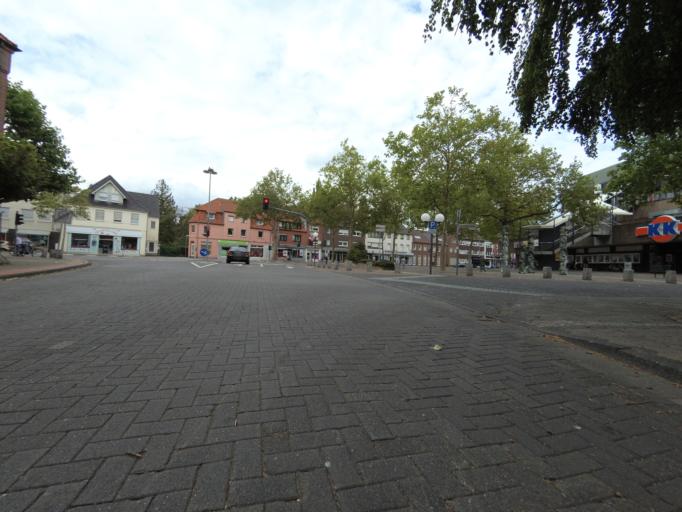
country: DE
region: North Rhine-Westphalia
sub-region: Regierungsbezirk Munster
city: Ahaus
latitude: 52.0769
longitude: 7.0091
